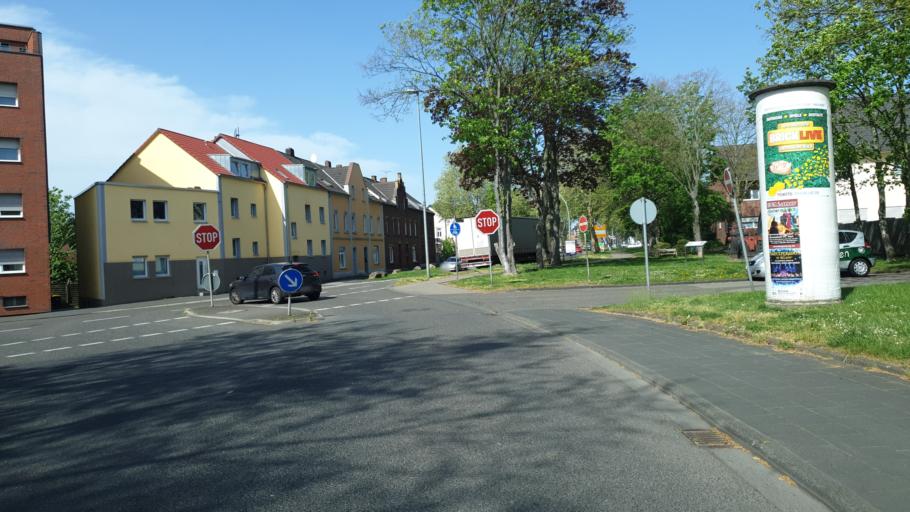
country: DE
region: North Rhine-Westphalia
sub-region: Regierungsbezirk Koln
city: Bergheim
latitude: 50.9364
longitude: 6.6964
